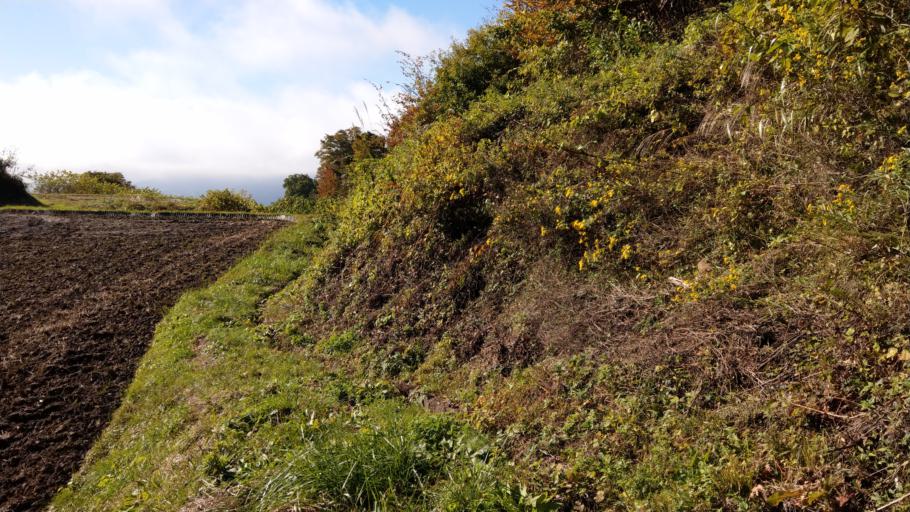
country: JP
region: Nagano
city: Komoro
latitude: 36.3589
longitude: 138.4260
